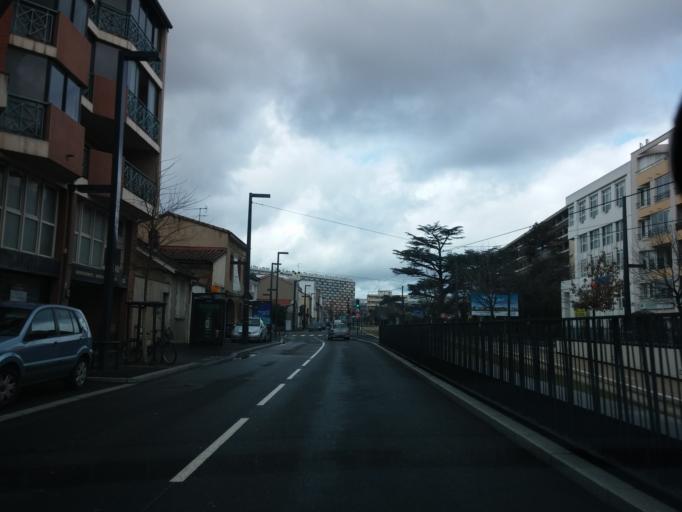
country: FR
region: Midi-Pyrenees
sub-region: Departement de la Haute-Garonne
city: Toulouse
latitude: 43.5890
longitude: 1.4227
